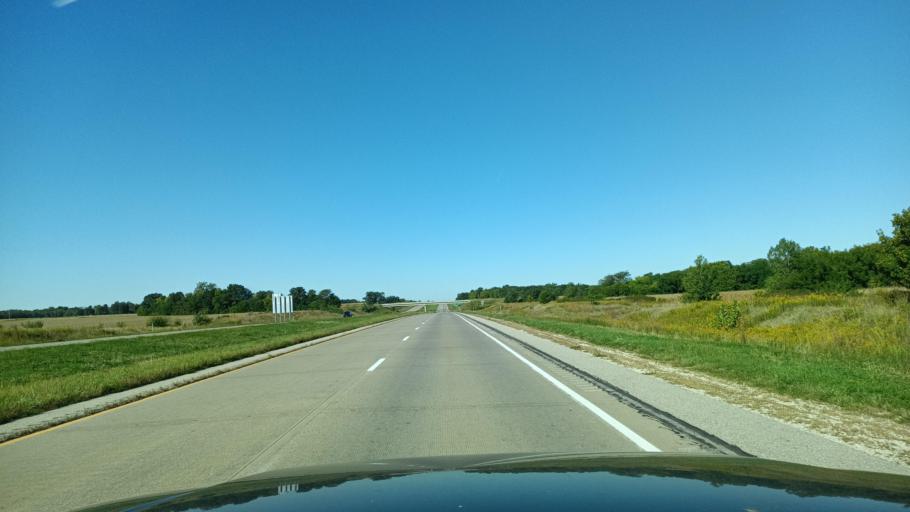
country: US
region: Iowa
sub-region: Lee County
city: Fort Madison
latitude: 40.6707
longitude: -91.2947
